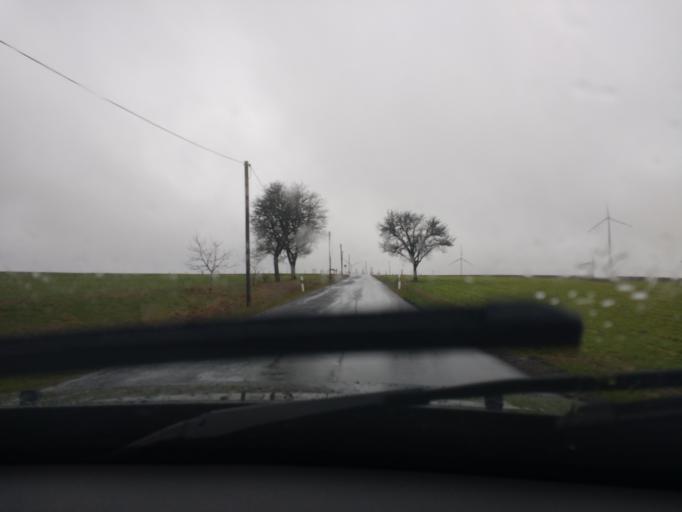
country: DE
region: Rheinland-Pfalz
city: Lampaden
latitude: 49.6557
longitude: 6.6917
